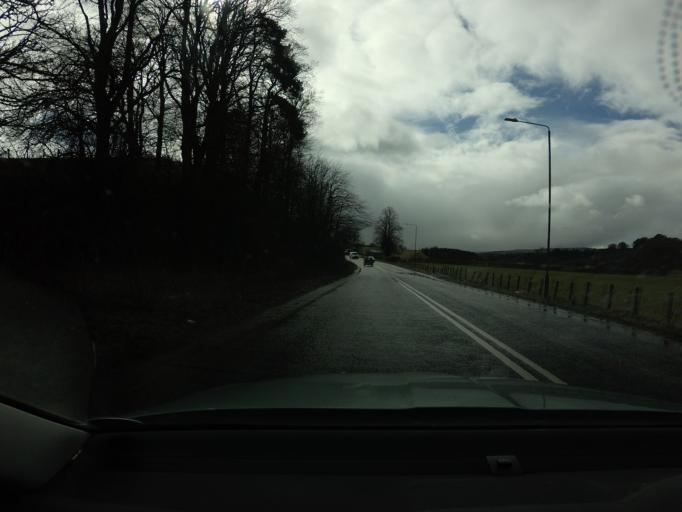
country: GB
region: Scotland
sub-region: South Lanarkshire
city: Douglas
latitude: 55.5830
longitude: -3.8046
